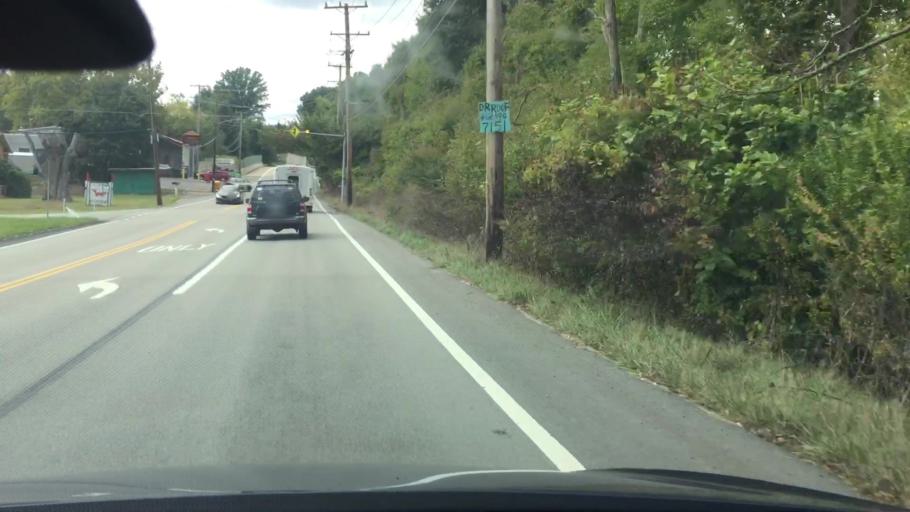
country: US
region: Pennsylvania
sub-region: Allegheny County
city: Cheswick
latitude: 40.5270
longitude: -79.8180
